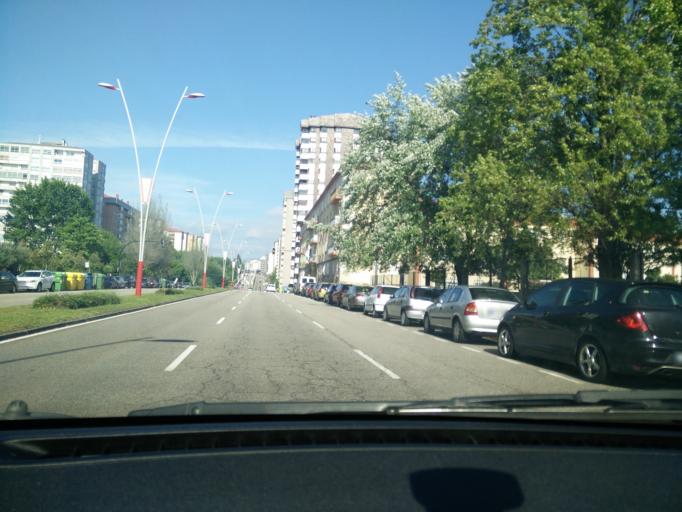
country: ES
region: Galicia
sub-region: Provincia de Pontevedra
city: Vigo
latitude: 42.2172
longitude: -8.7527
